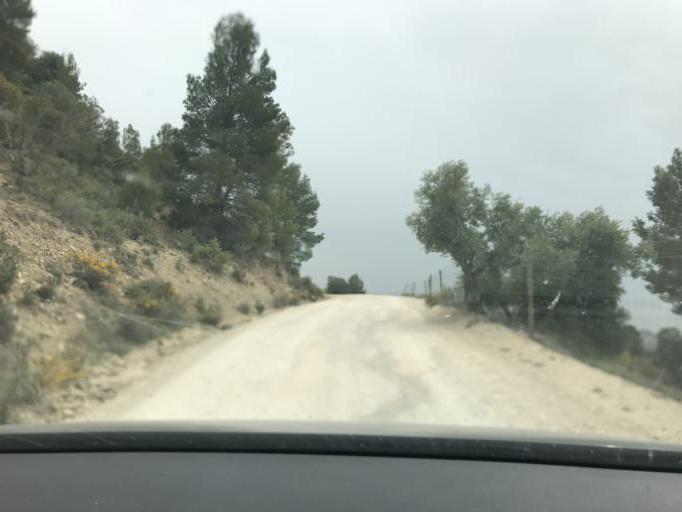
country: ES
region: Andalusia
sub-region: Provincia de Granada
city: Castril
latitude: 37.8286
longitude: -2.7726
